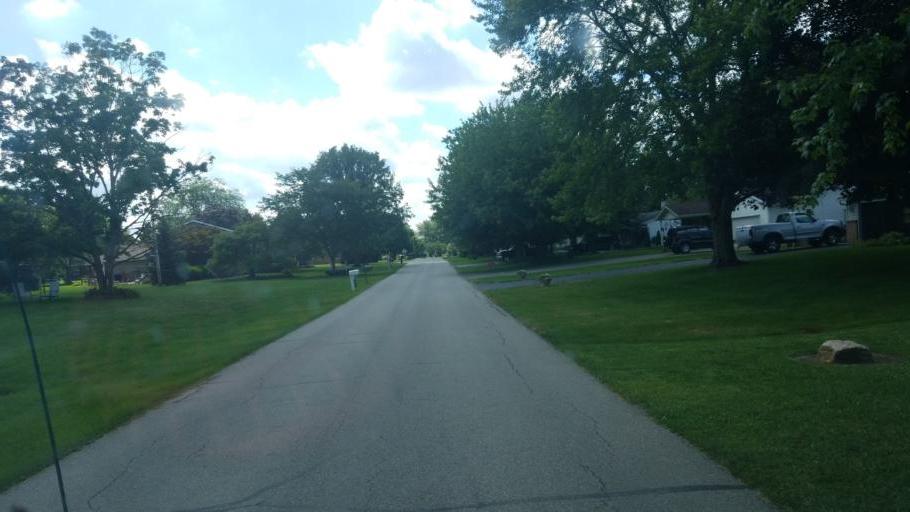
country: US
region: Ohio
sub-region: Marion County
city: Marion
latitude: 40.5325
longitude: -83.0925
